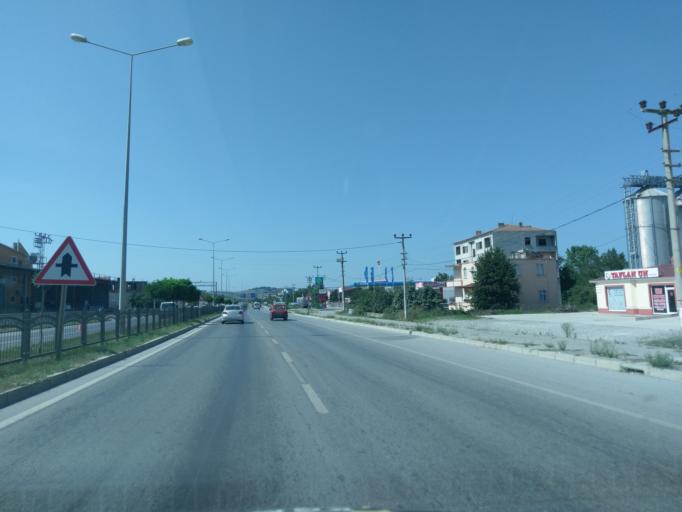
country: TR
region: Samsun
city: Bafra
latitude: 41.5685
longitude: 35.8784
